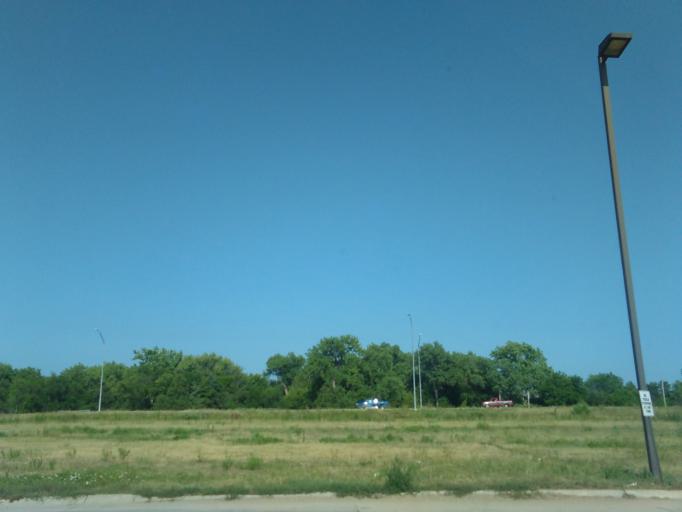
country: US
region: Nebraska
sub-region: Hall County
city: Grand Island
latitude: 40.8303
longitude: -98.3799
